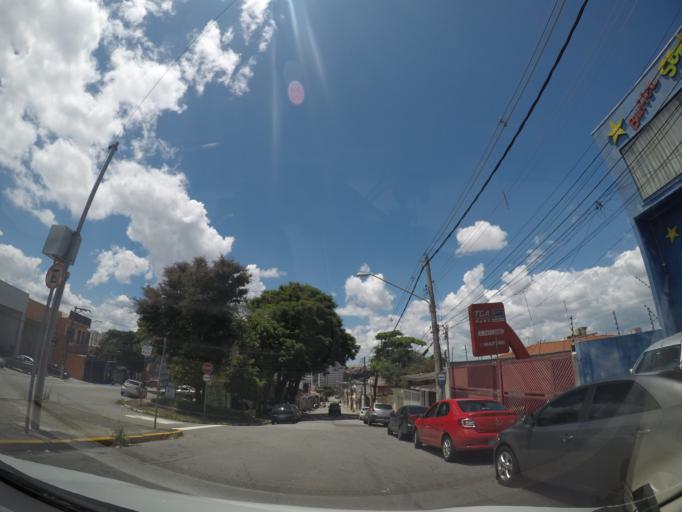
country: BR
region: Sao Paulo
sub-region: Guarulhos
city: Guarulhos
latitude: -23.4493
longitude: -46.5401
